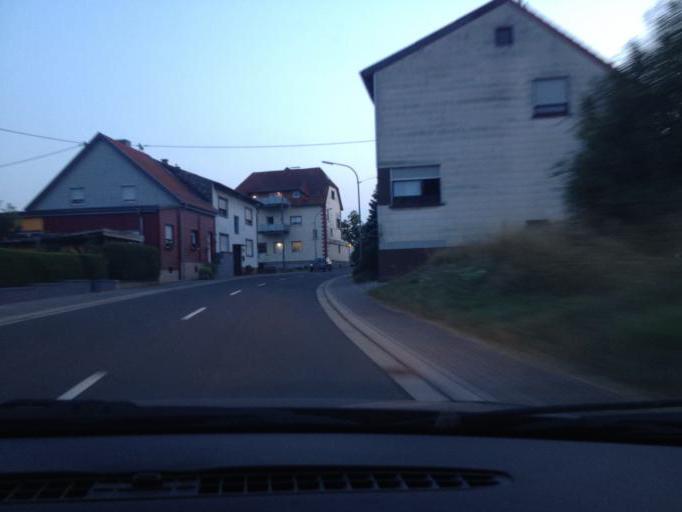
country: DE
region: Saarland
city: Namborn
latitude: 49.5389
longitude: 7.1211
